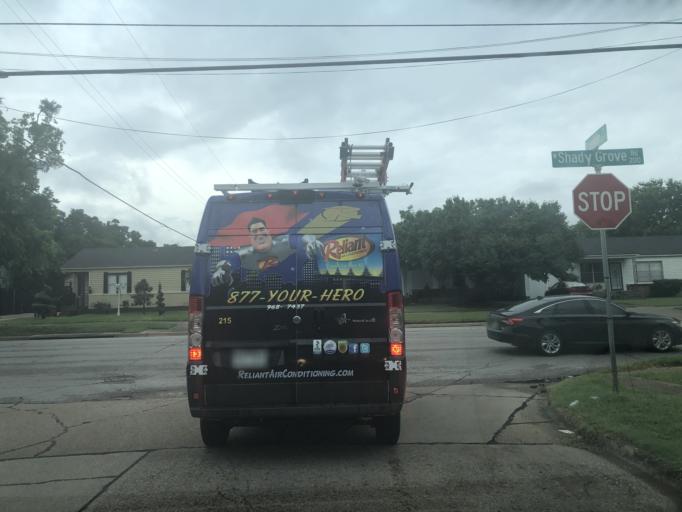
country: US
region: Texas
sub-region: Dallas County
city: Irving
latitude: 32.8010
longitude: -96.9496
